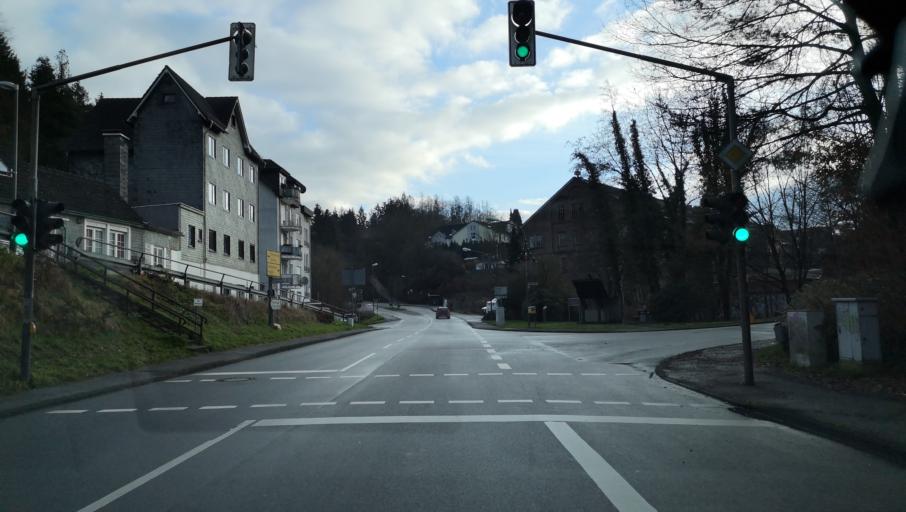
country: DE
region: North Rhine-Westphalia
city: Radevormwald
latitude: 51.2156
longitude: 7.3095
